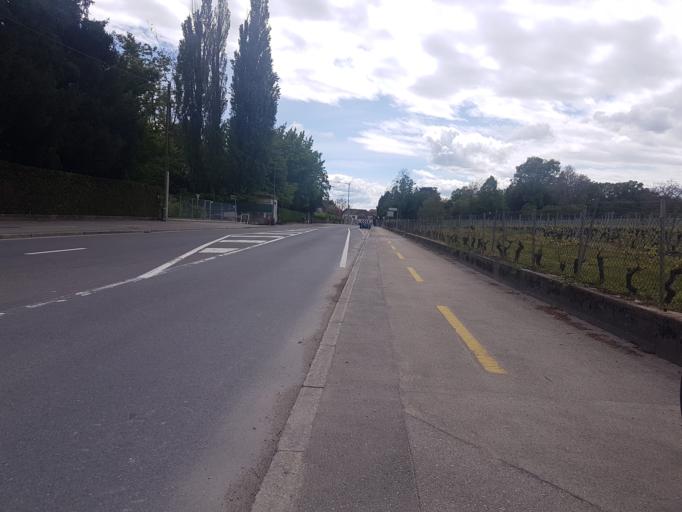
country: CH
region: Vaud
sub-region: Nyon District
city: Coppet
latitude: 46.3206
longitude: 6.1959
